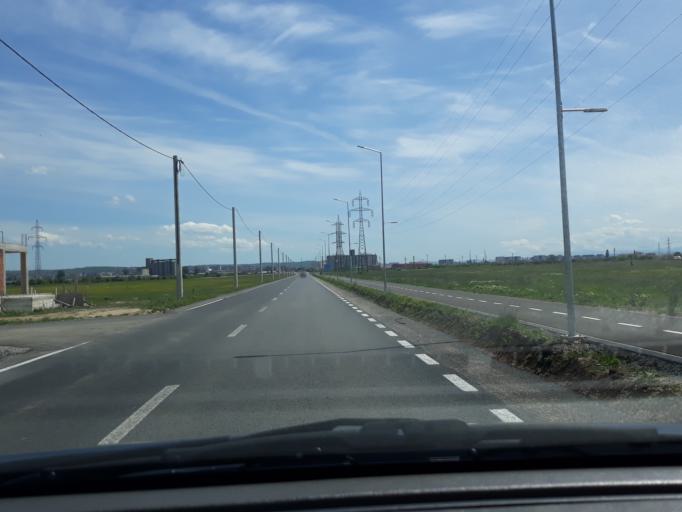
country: RO
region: Bihor
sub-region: Comuna Santandrei
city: Santandrei
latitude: 47.0671
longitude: 21.8704
